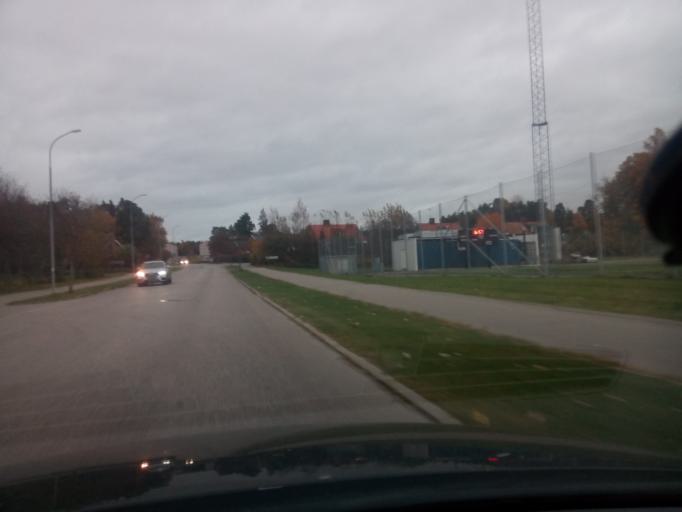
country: SE
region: Soedermanland
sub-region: Nykopings Kommun
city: Nykoping
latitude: 58.7495
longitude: 17.0431
